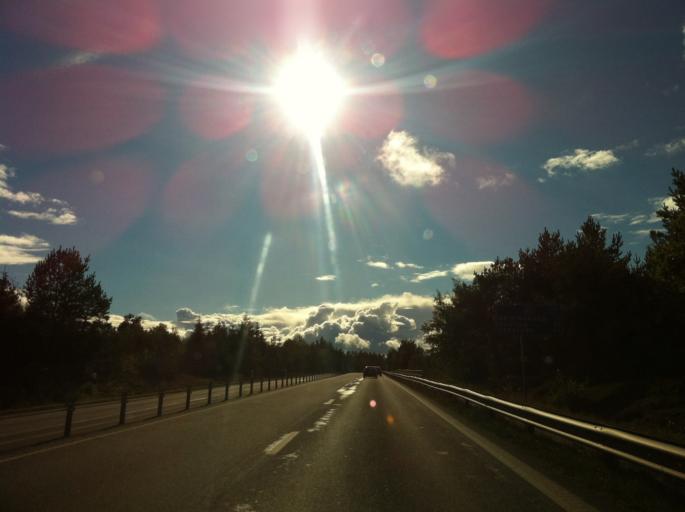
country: SE
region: Skane
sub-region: Hassleholms Kommun
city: Sosdala
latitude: 56.1618
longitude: 13.5738
